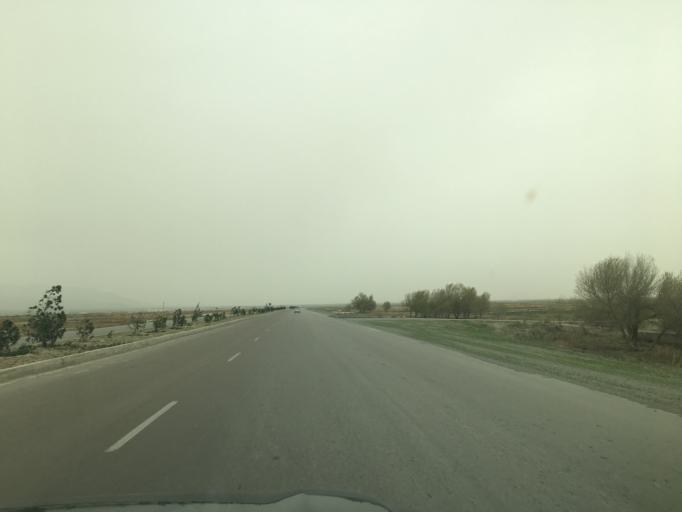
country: TM
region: Ahal
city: Baharly
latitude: 38.3580
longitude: 57.5370
